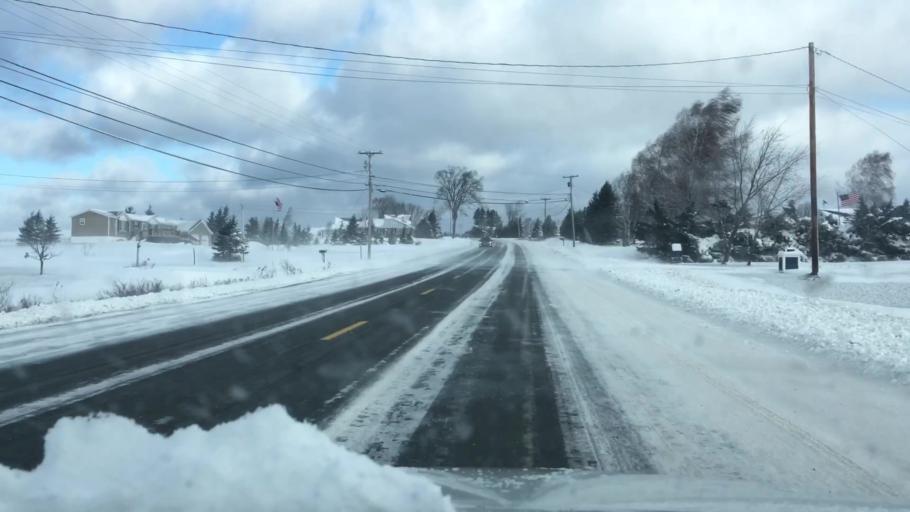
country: US
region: Maine
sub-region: Aroostook County
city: Caribou
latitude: 46.8992
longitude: -68.0154
